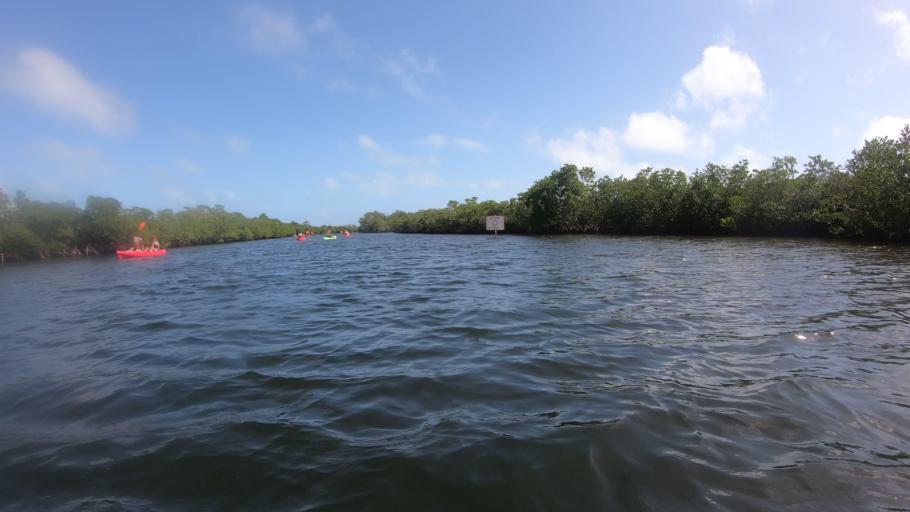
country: US
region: Florida
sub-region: Monroe County
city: Key Largo
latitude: 25.1228
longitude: -80.4054
